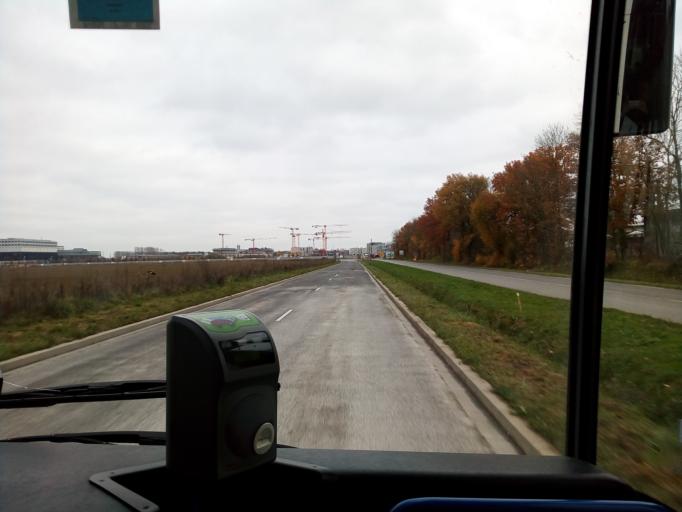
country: FR
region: Ile-de-France
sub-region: Departement de l'Essonne
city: Orsay
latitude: 48.7141
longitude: 2.1873
